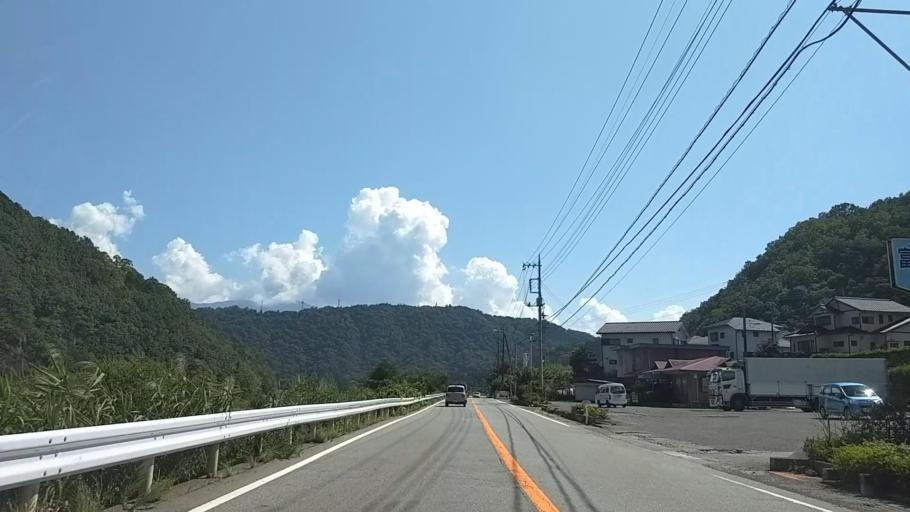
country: JP
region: Yamanashi
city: Ryuo
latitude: 35.5220
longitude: 138.4516
